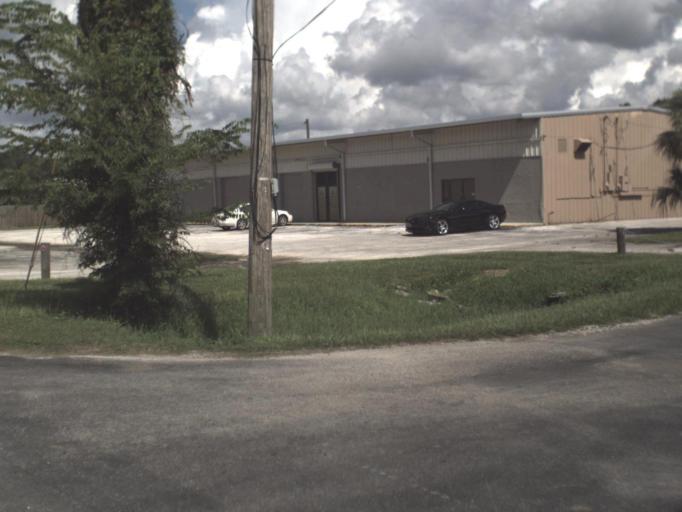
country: US
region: Florida
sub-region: Hillsborough County
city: East Lake-Orient Park
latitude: 27.9668
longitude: -82.3831
